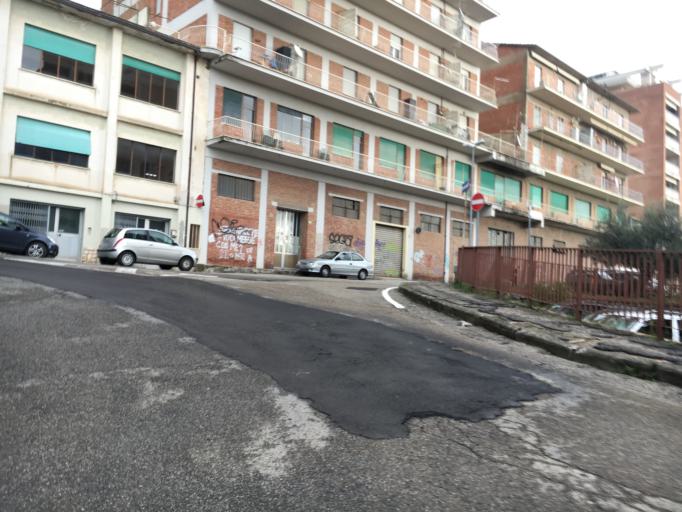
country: IT
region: Umbria
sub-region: Provincia di Perugia
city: Perugia
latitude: 43.1164
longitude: 12.3771
